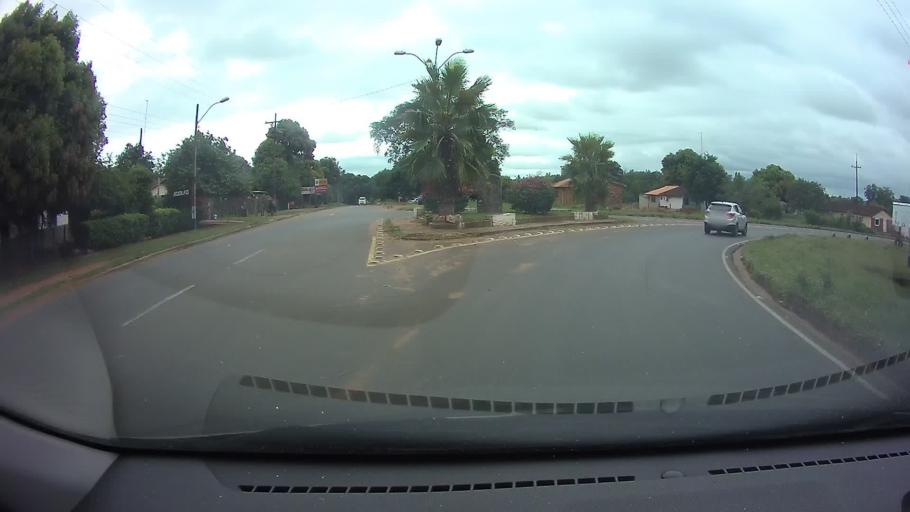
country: PY
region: Central
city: Nueva Italia
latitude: -25.6103
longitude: -57.4615
